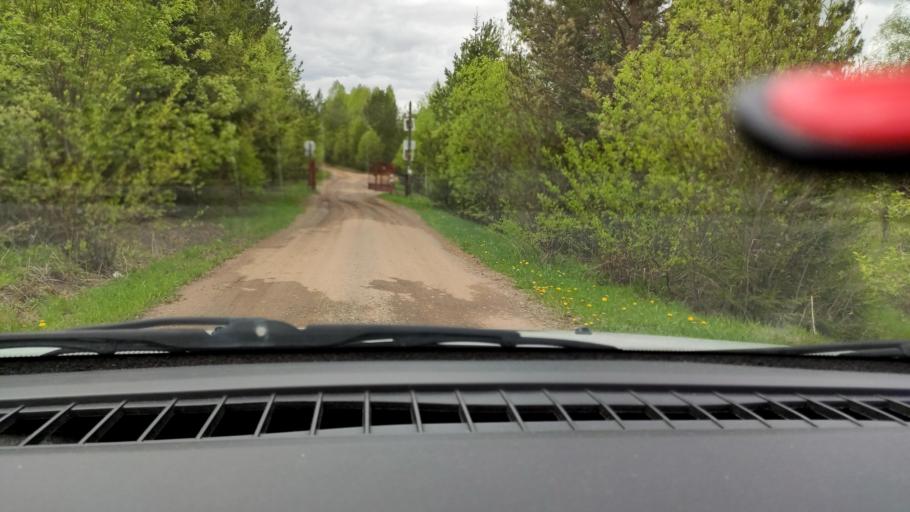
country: RU
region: Perm
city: Bershet'
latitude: 57.7224
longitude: 56.4064
